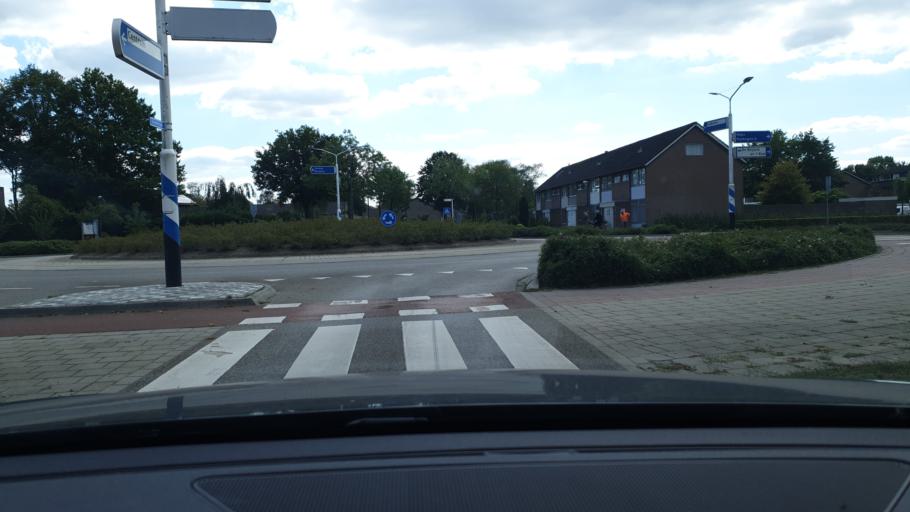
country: NL
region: North Brabant
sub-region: Gemeente Cuijk
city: Cuijk
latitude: 51.7216
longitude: 5.8873
